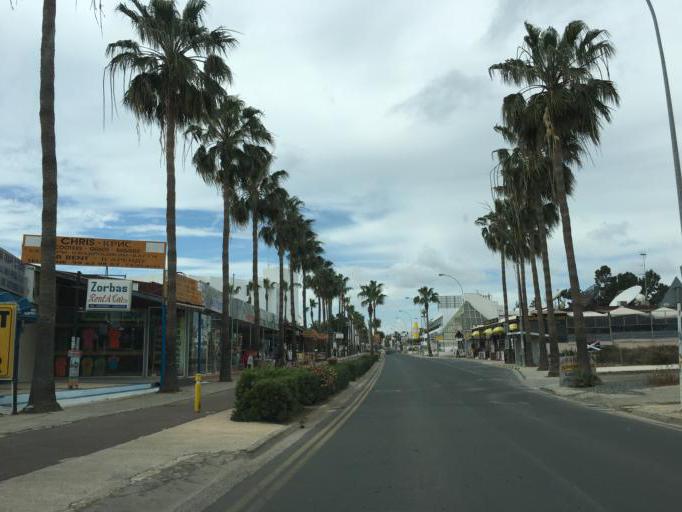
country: CY
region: Ammochostos
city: Ayia Napa
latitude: 34.9866
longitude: 34.0072
